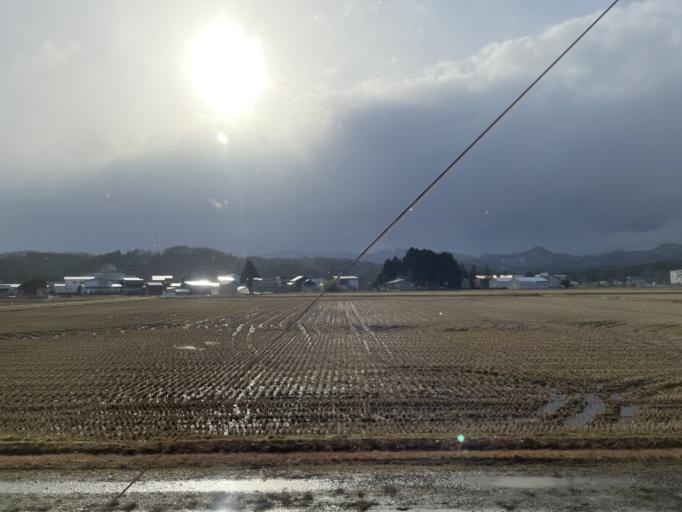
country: JP
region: Aomori
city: Aomori Shi
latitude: 41.0535
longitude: 140.5934
